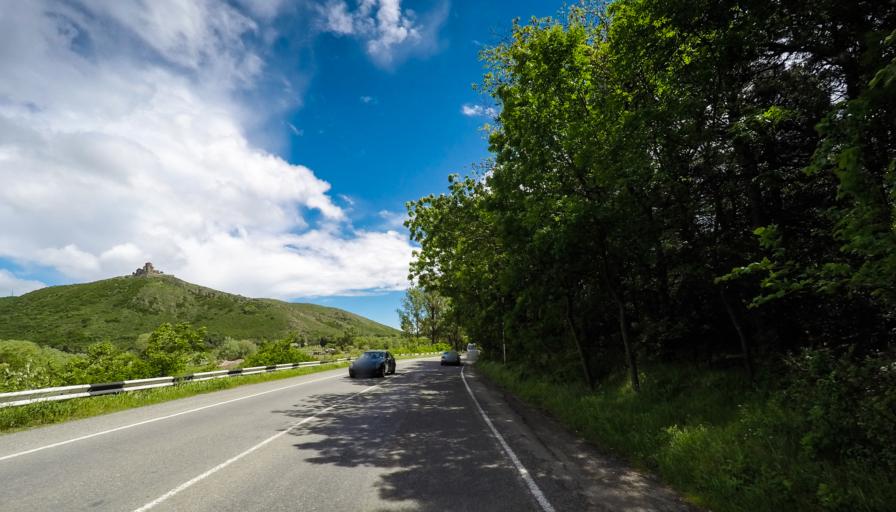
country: GE
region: Mtskheta-Mtianeti
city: Mtskheta
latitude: 41.8388
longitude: 44.7223
